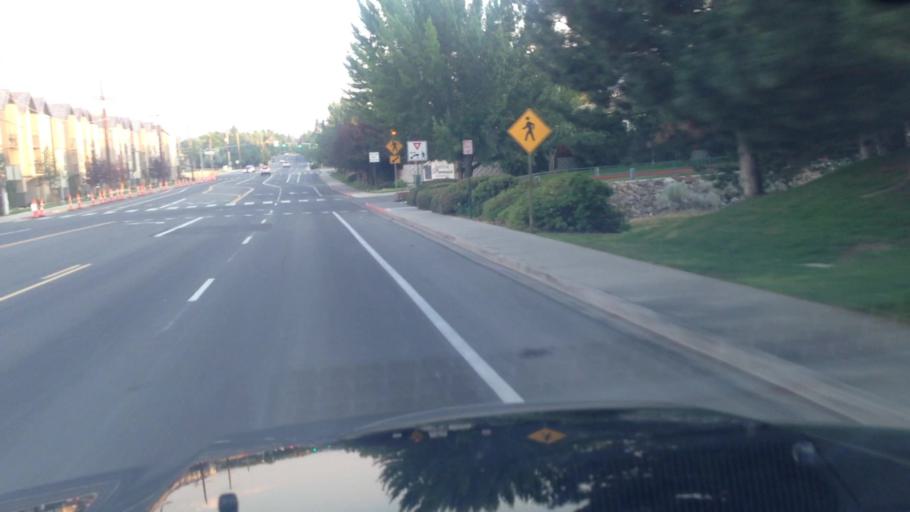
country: US
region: Nevada
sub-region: Washoe County
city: Reno
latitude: 39.4931
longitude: -119.8127
